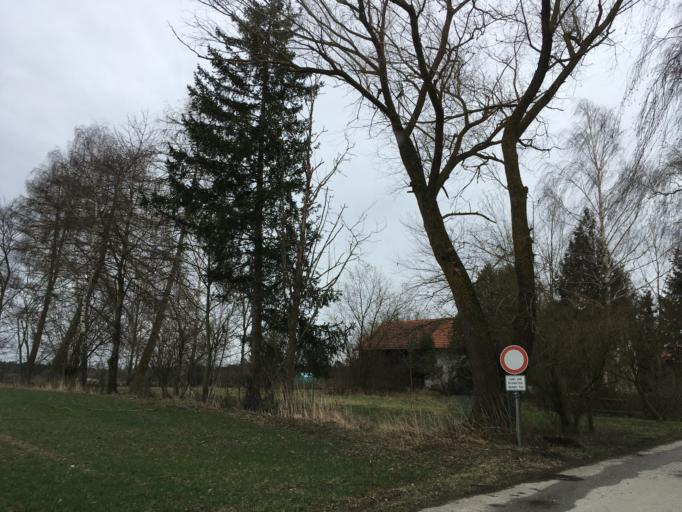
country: DE
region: Bavaria
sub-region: Upper Bavaria
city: Ampfing
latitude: 48.2415
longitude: 12.4222
